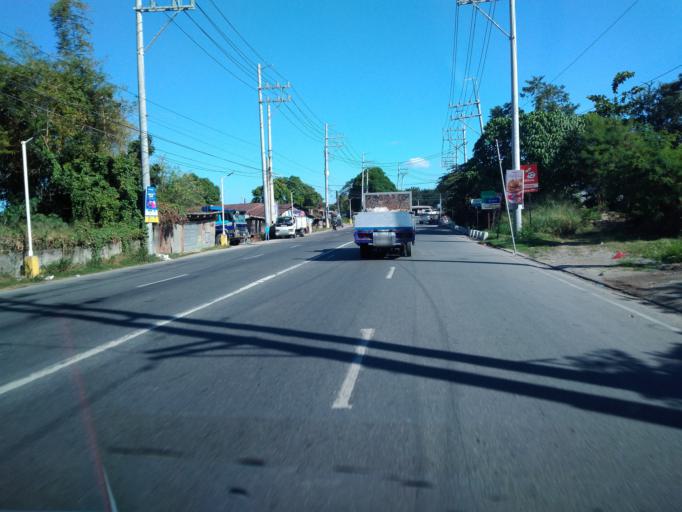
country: PH
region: Central Luzon
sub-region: Province of Bulacan
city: Santa Maria
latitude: 14.8154
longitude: 120.9488
